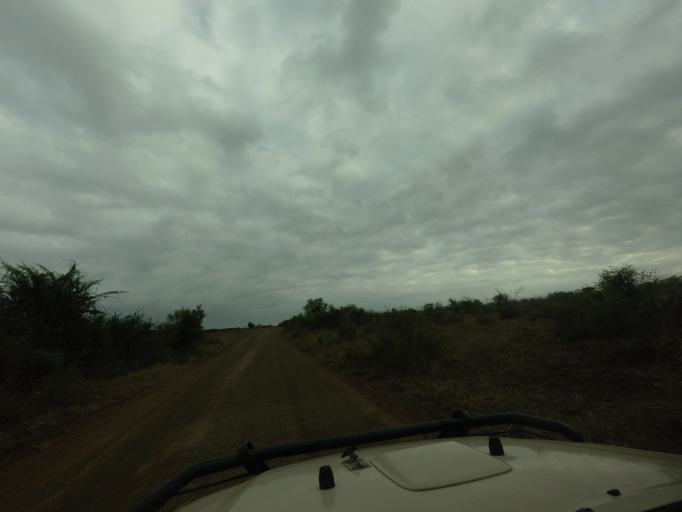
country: ZA
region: Mpumalanga
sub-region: Ehlanzeni District
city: Komatipoort
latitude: -25.3227
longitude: 31.9067
